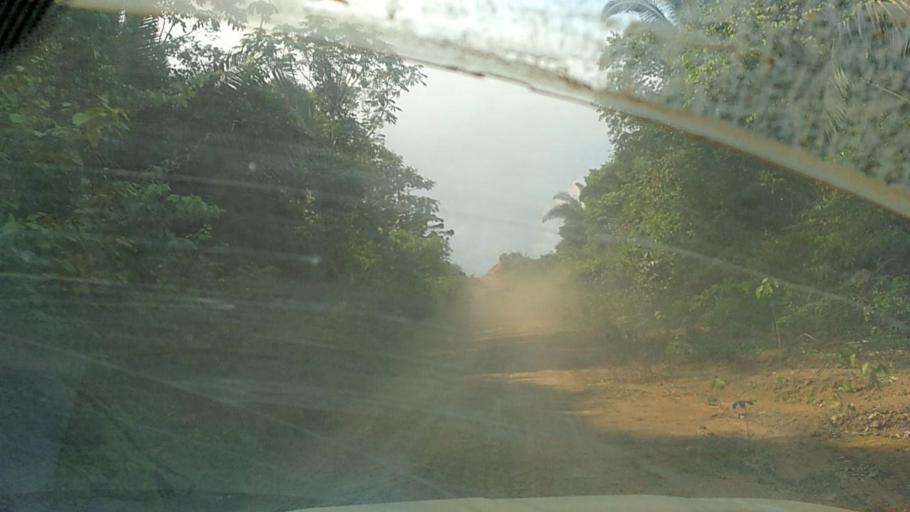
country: BR
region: Rondonia
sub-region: Porto Velho
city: Porto Velho
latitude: -8.6958
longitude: -63.2393
